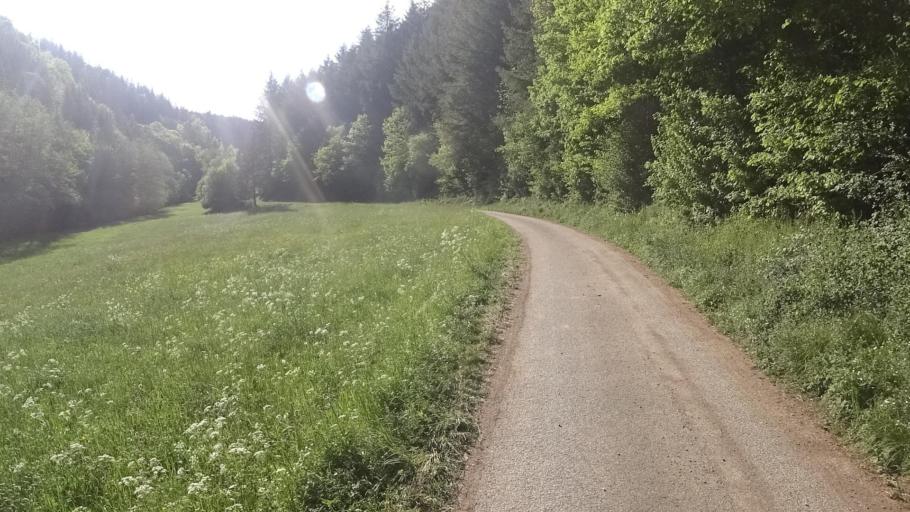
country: DE
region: Rheinland-Pfalz
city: Lind
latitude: 50.4917
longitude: 6.9071
